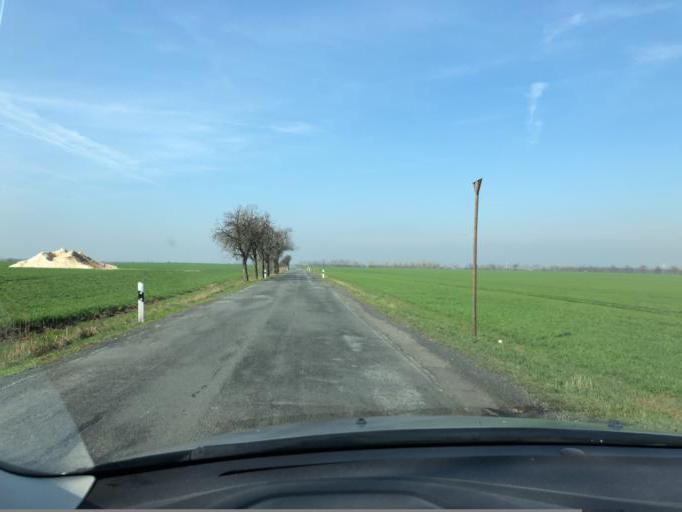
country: DE
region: Saxony
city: Rackwitz
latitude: 51.4233
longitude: 12.4177
